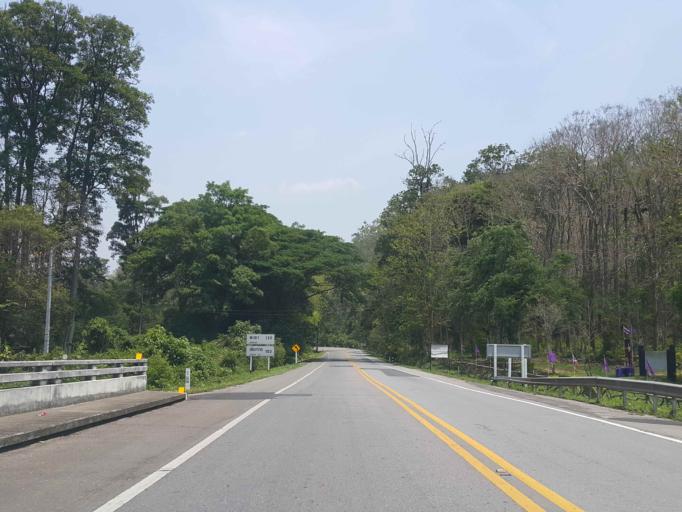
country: TH
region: Chiang Mai
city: Mae On
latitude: 18.9351
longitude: 99.2383
